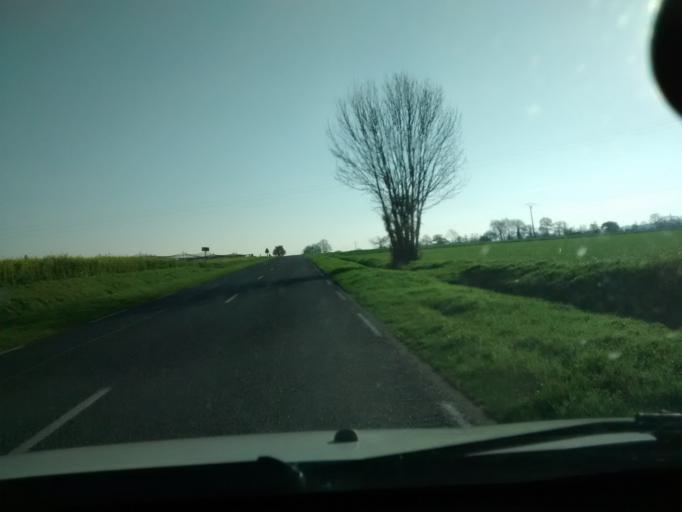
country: FR
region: Lower Normandy
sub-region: Departement de la Manche
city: Pontorson
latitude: 48.5219
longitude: -1.4828
